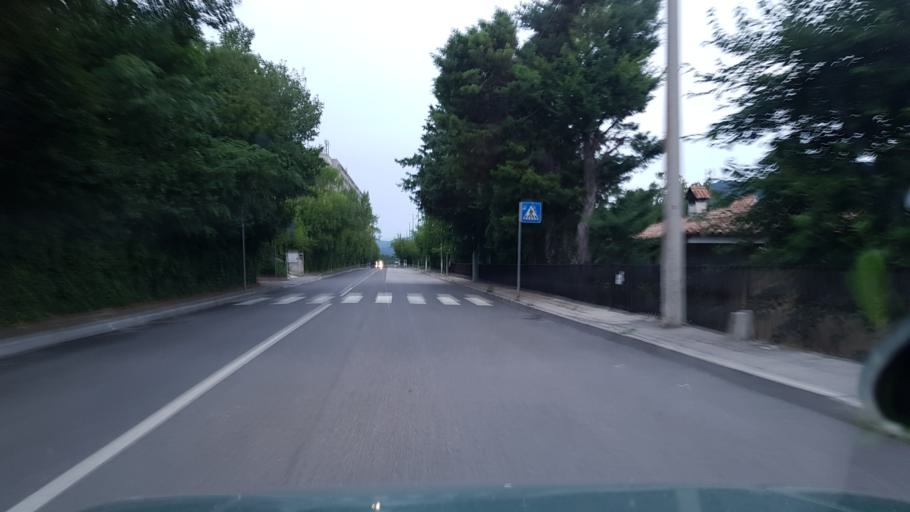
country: IT
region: Friuli Venezia Giulia
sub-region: Provincia di Trieste
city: Domio
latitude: 45.6380
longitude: 13.8293
